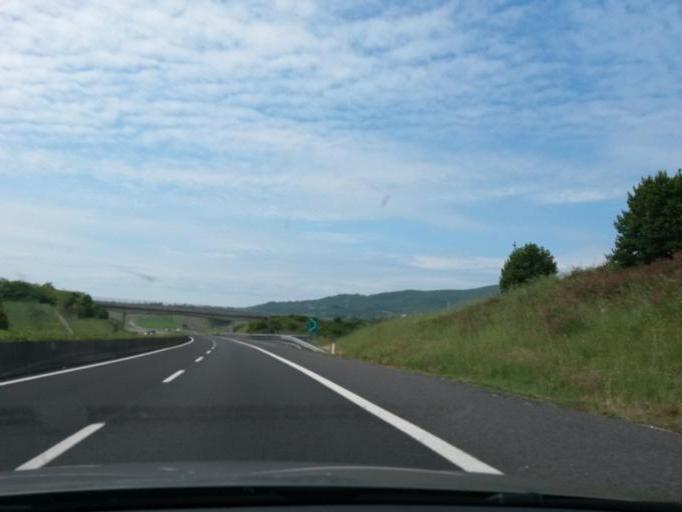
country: IT
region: Tuscany
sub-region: Provincia di Livorno
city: Collesalvetti
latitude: 43.5416
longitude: 10.4678
